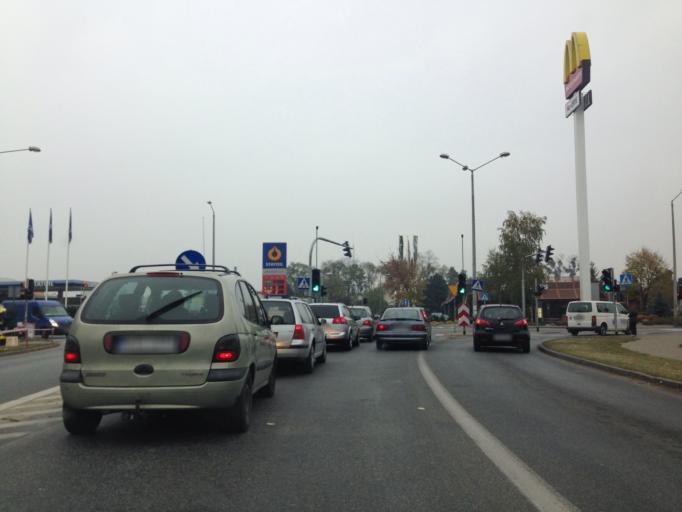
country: PL
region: Kujawsko-Pomorskie
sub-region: Powiat brodnicki
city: Brodnica
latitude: 53.2595
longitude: 19.3959
